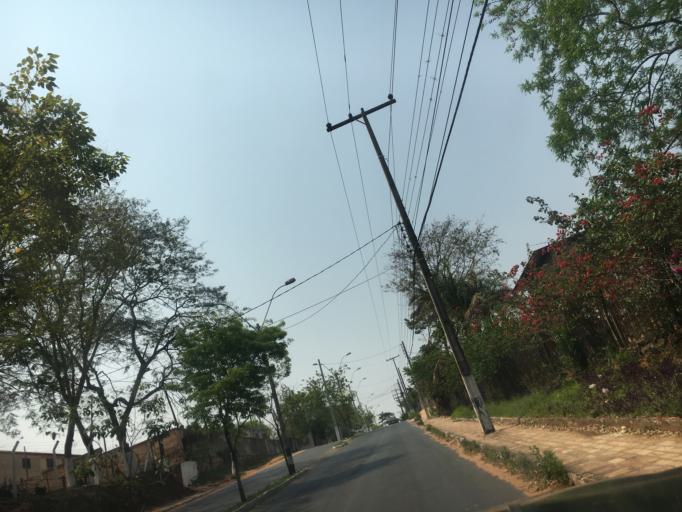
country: PY
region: Central
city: Villa Elisa
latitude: -25.3794
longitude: -57.5901
